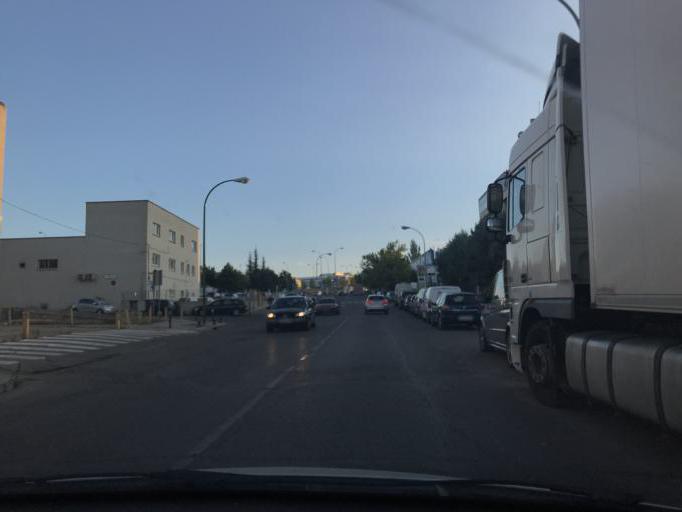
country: ES
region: Madrid
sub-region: Provincia de Madrid
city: Alcobendas
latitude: 40.5346
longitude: -3.6568
